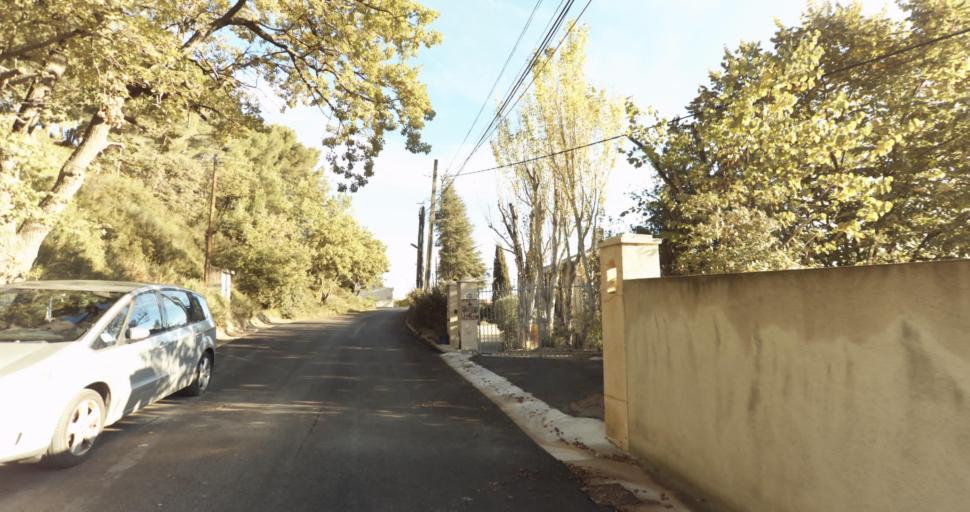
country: FR
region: Provence-Alpes-Cote d'Azur
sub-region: Departement des Bouches-du-Rhone
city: Venelles
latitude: 43.6050
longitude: 5.4792
